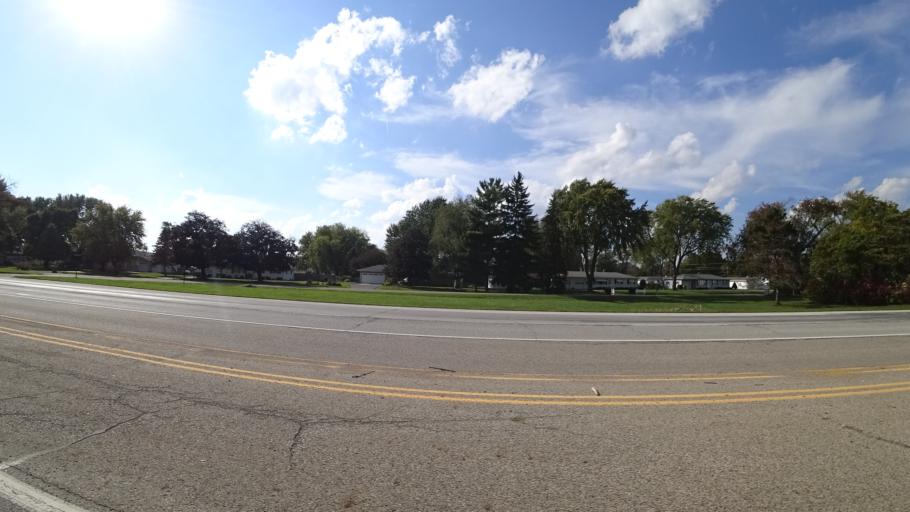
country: US
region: Michigan
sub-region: Saint Joseph County
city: Three Rivers
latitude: 41.9465
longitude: -85.6509
